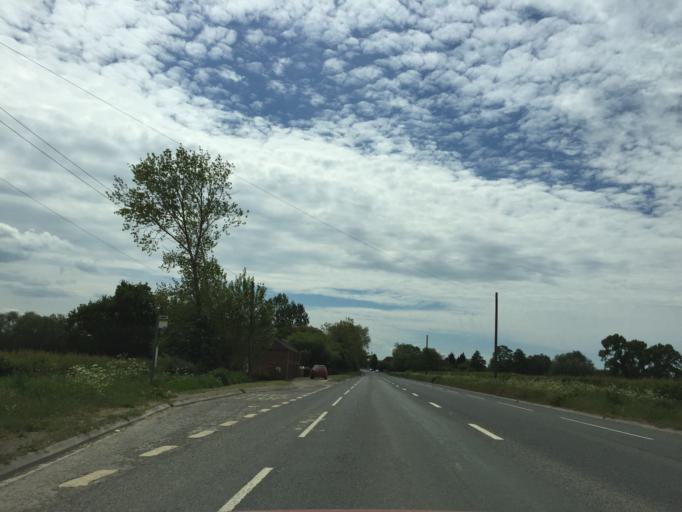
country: GB
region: England
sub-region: Gloucestershire
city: Stonehouse
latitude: 51.7863
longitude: -2.3131
